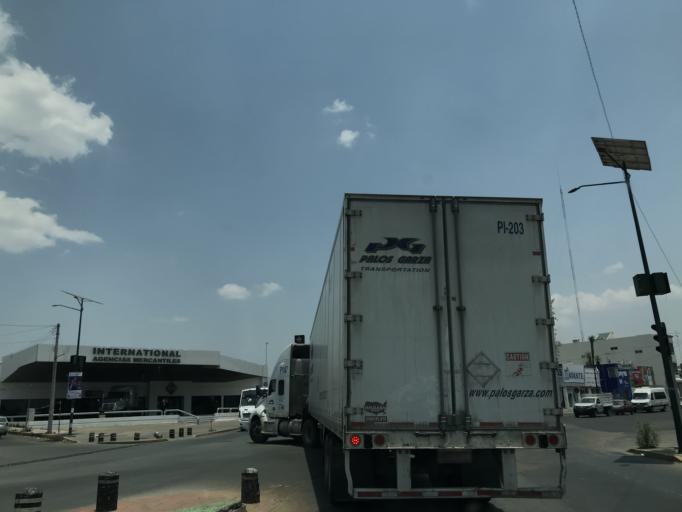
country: MX
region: Tlaxcala
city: Apizaco
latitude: 19.4177
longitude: -98.1519
